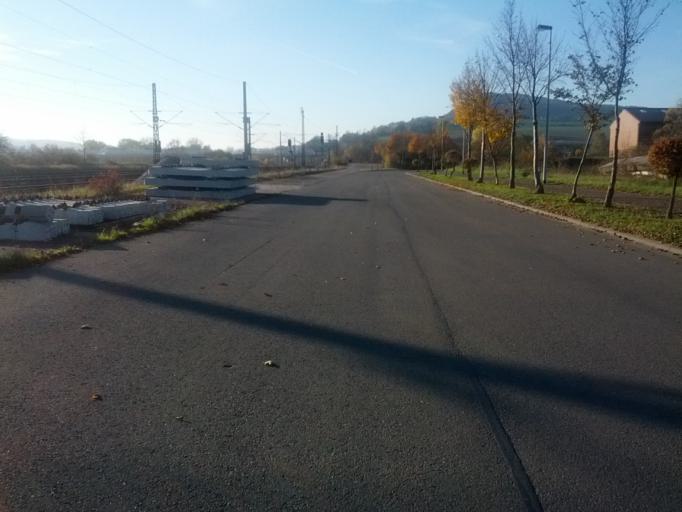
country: DE
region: Thuringia
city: Mechterstadt
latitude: 50.9460
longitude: 10.4959
